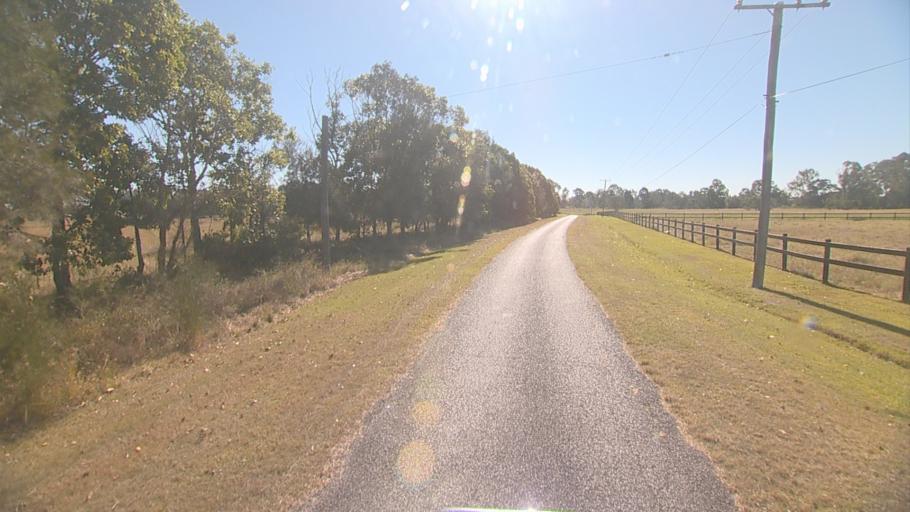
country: AU
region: Queensland
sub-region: Logan
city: Waterford West
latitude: -27.7042
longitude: 153.1300
